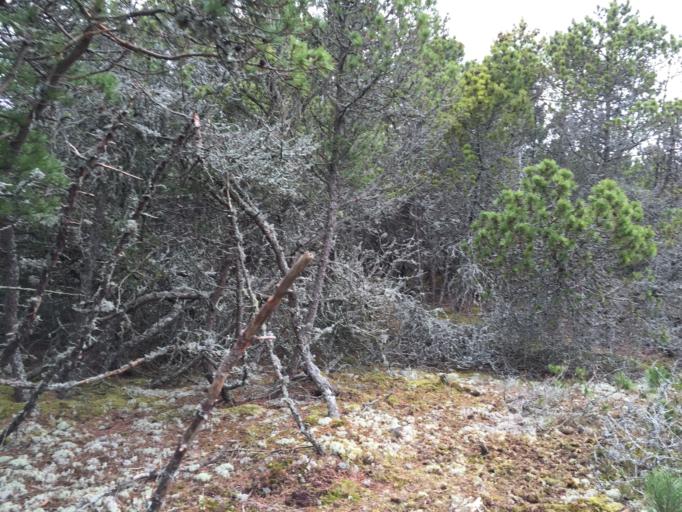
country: LT
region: Klaipedos apskritis
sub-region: Klaipeda
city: Klaipeda
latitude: 55.5605
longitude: 21.1229
